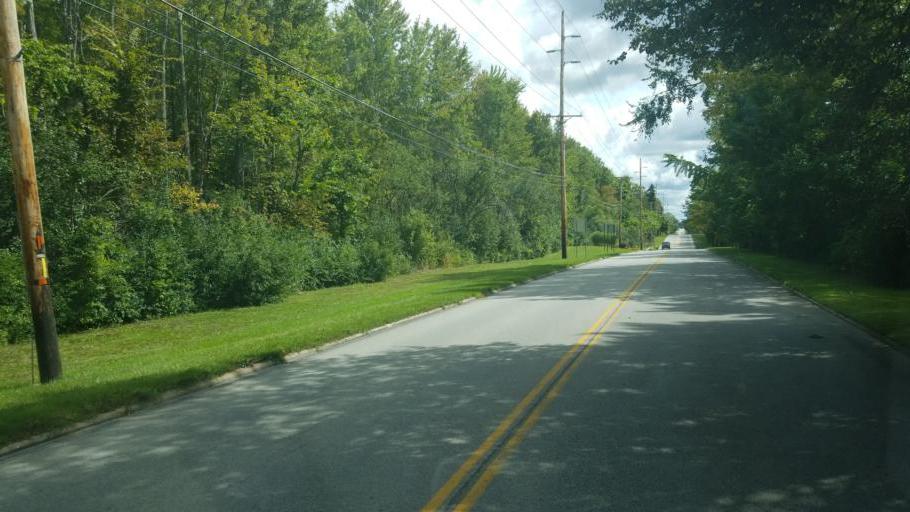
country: US
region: Ohio
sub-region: Lorain County
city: Oberlin
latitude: 41.2939
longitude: -82.1940
